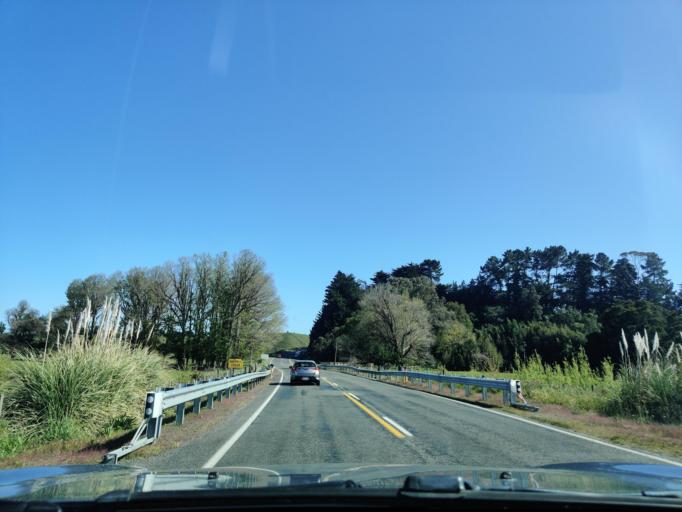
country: NZ
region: Manawatu-Wanganui
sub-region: Rangitikei District
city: Bulls
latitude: -40.0622
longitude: 175.2224
